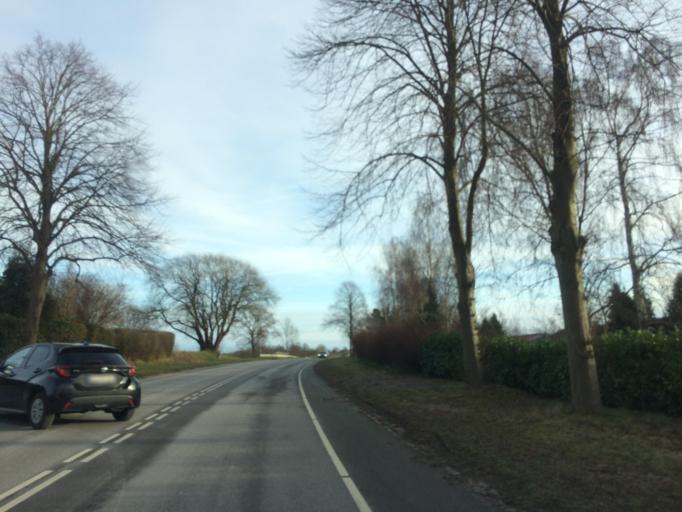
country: DK
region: Capital Region
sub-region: Fredensborg Kommune
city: Fredensborg
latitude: 55.9666
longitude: 12.4174
